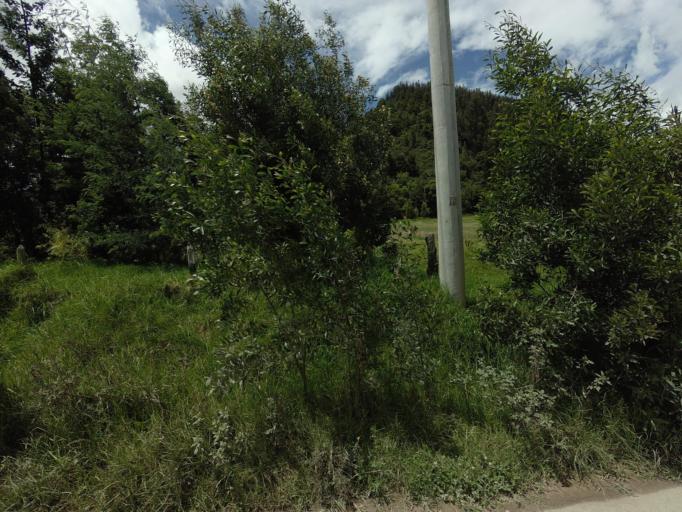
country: CO
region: Cundinamarca
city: Tabio
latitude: 4.9278
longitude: -74.0679
